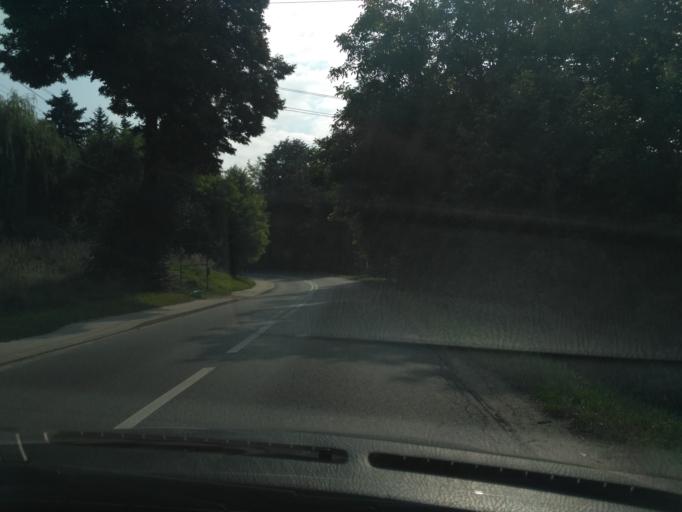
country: PL
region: Subcarpathian Voivodeship
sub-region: Powiat rzeszowski
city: Boguchwala
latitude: 50.0031
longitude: 21.9368
